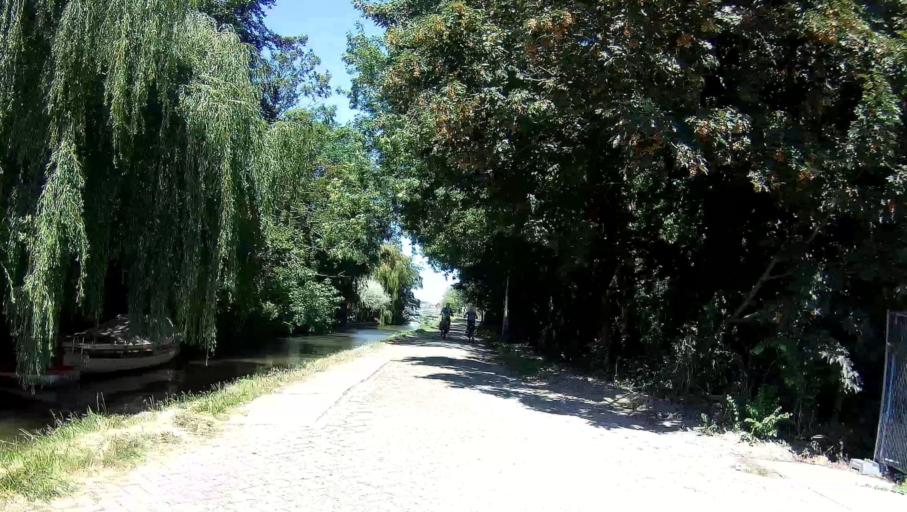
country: NL
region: South Holland
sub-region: Gemeente Westland
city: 's-Gravenzande
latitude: 52.0036
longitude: 4.1766
